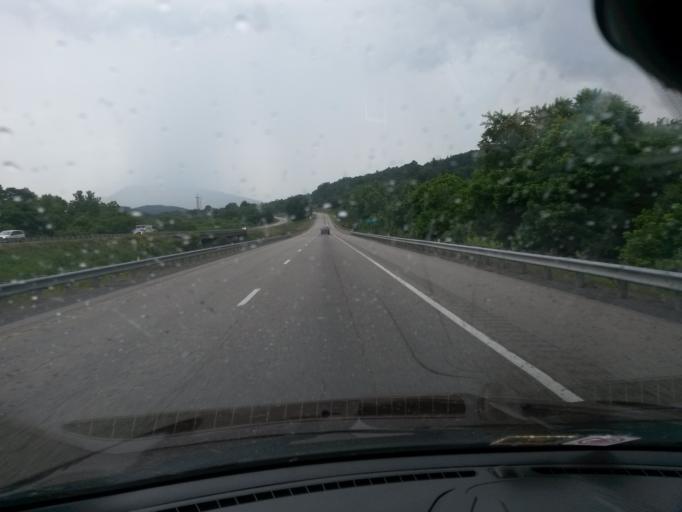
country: US
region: Virginia
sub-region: Rockbridge County
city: East Lexington
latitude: 37.8244
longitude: -79.4428
